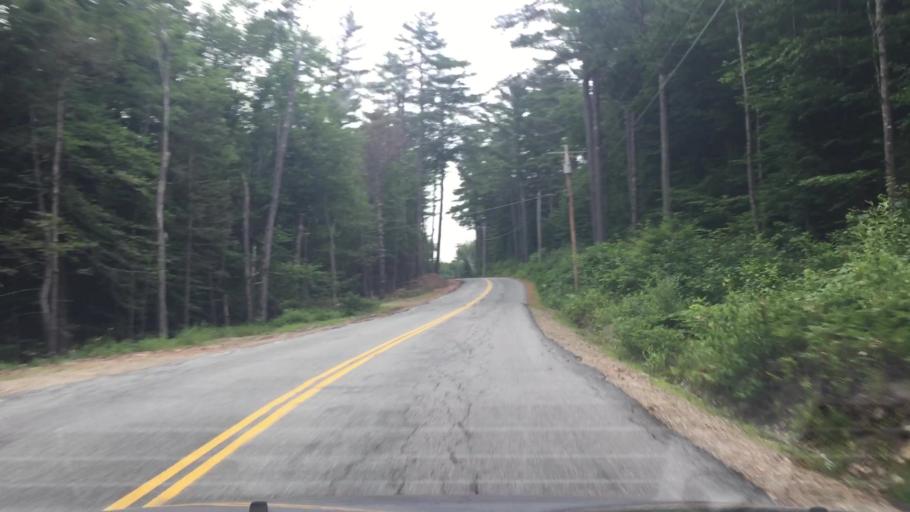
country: US
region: New Hampshire
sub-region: Carroll County
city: North Conway
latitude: 44.0987
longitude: -71.1919
